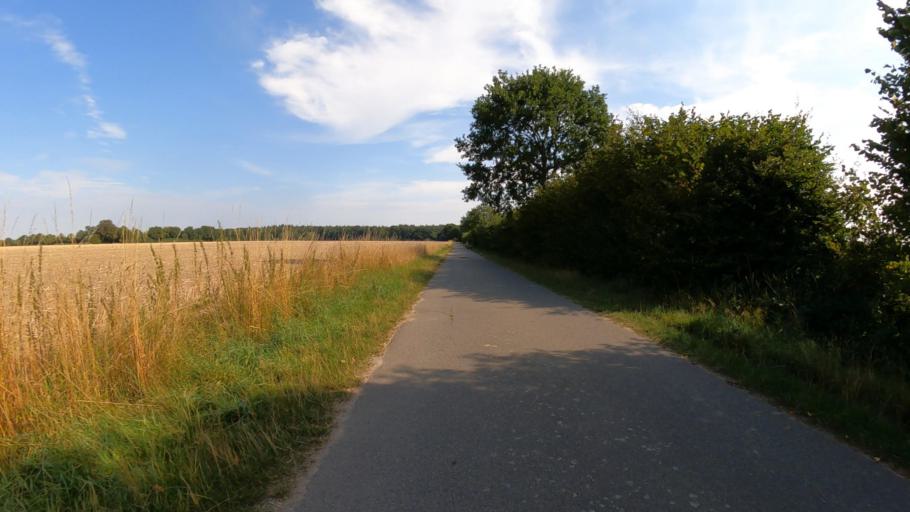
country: DE
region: Schleswig-Holstein
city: Dassendorf
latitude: 53.4962
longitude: 10.3853
